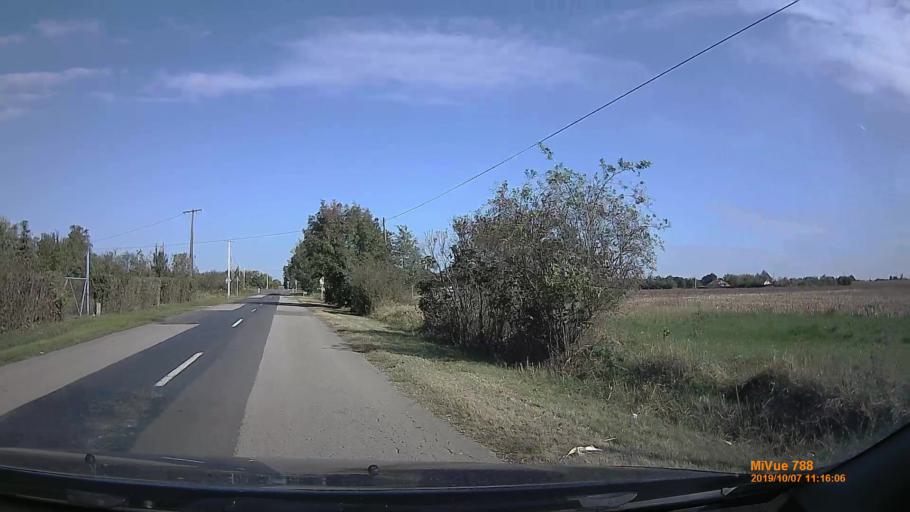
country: HU
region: Bekes
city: Kondoros
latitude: 46.7319
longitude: 20.7813
